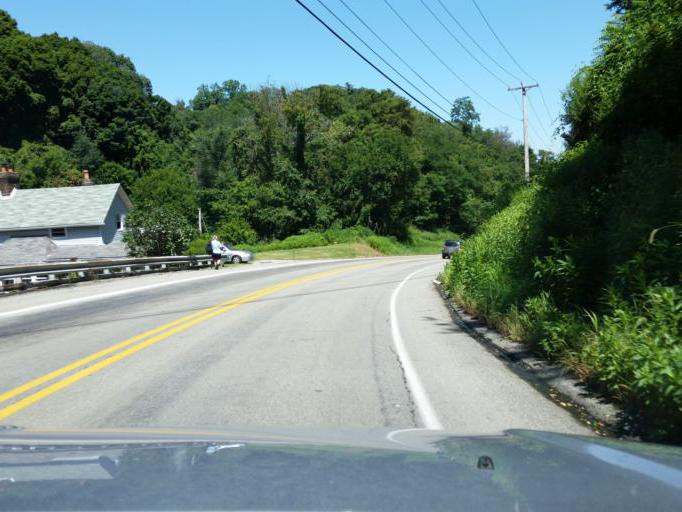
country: US
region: Pennsylvania
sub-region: Allegheny County
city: Churchill
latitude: 40.4647
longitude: -79.8466
